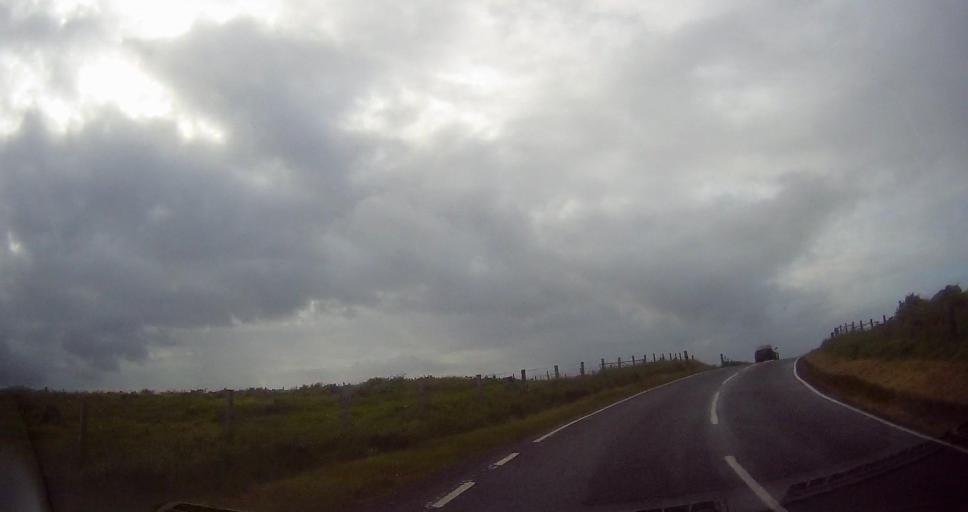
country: GB
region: Scotland
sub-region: Orkney Islands
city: Stromness
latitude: 58.9209
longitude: -3.1969
